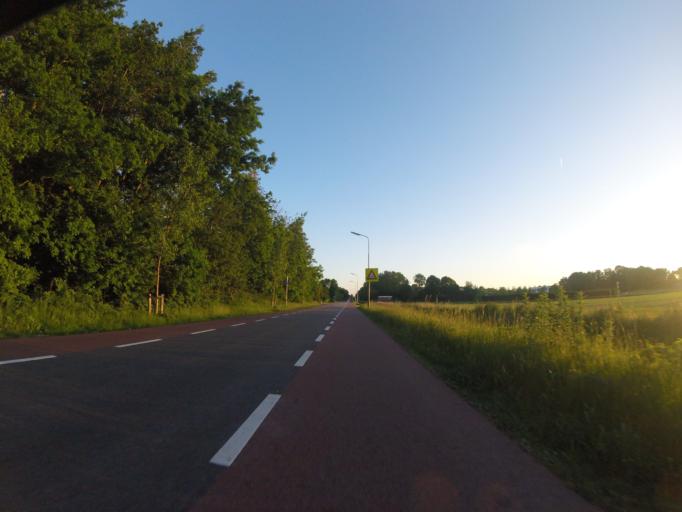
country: NL
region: North Holland
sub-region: Gemeente Heemstede
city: Heemstede
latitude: 52.3345
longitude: 4.6550
